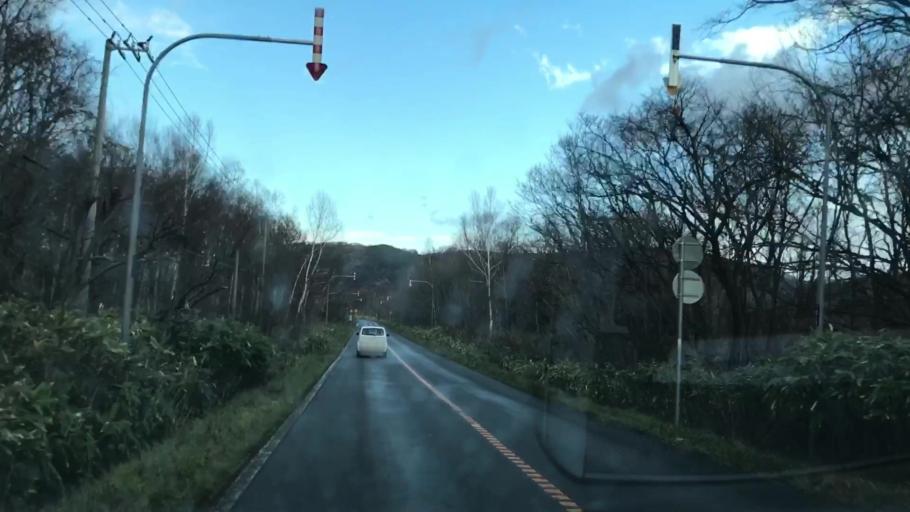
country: JP
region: Hokkaido
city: Yoichi
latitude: 43.3256
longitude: 140.5013
